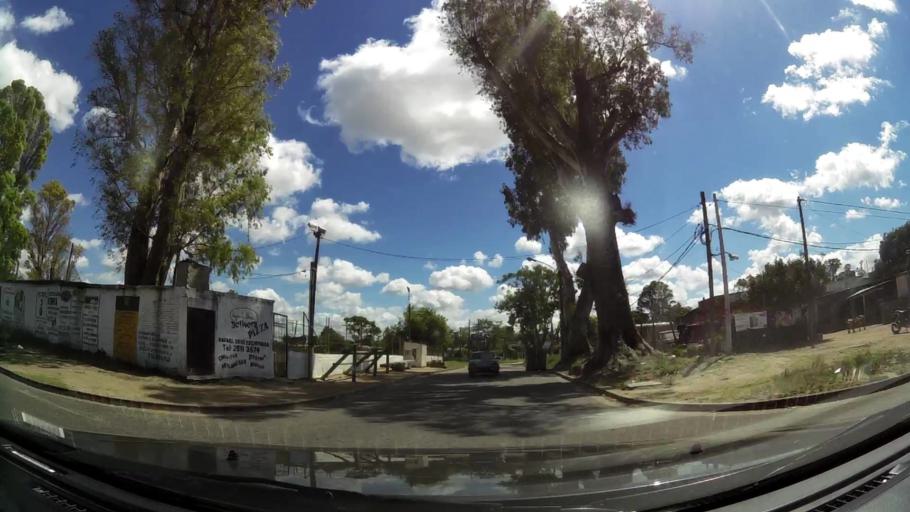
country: UY
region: Canelones
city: Paso de Carrasco
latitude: -34.8406
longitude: -56.1277
